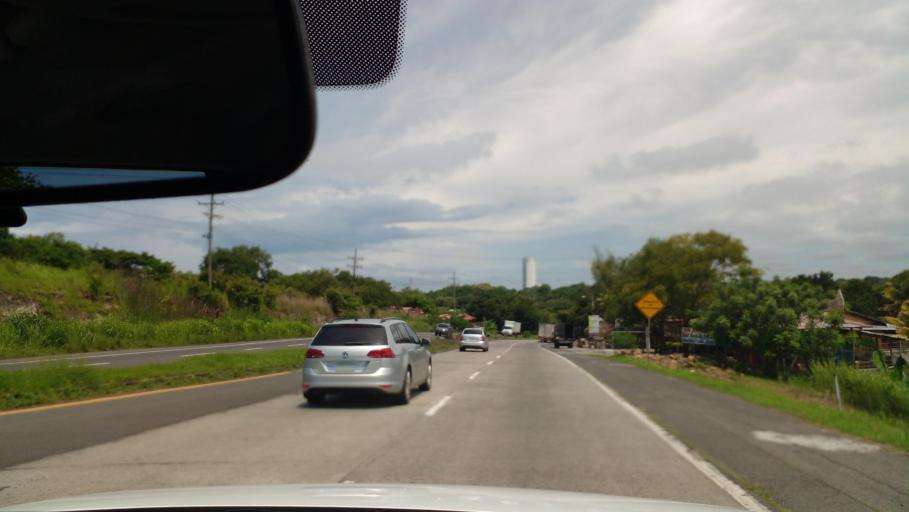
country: PA
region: Panama
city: Nueva Gorgona
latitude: 8.4805
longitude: -79.9582
